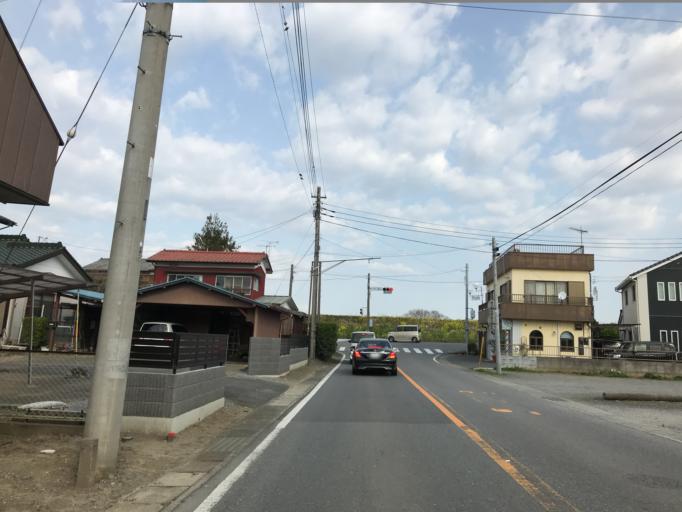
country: JP
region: Ibaraki
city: Mitsukaido
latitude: 36.0192
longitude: 140.0086
